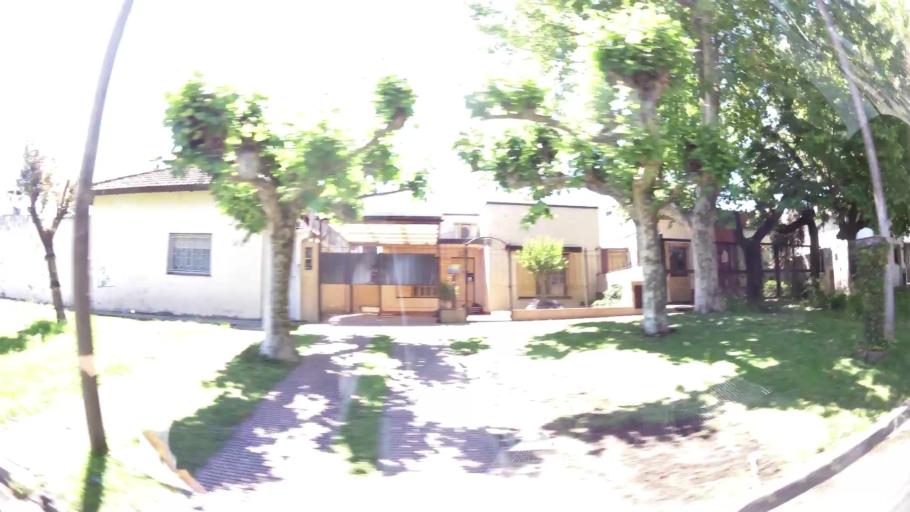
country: AR
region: Buenos Aires
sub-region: Partido de Quilmes
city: Quilmes
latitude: -34.7398
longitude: -58.2864
